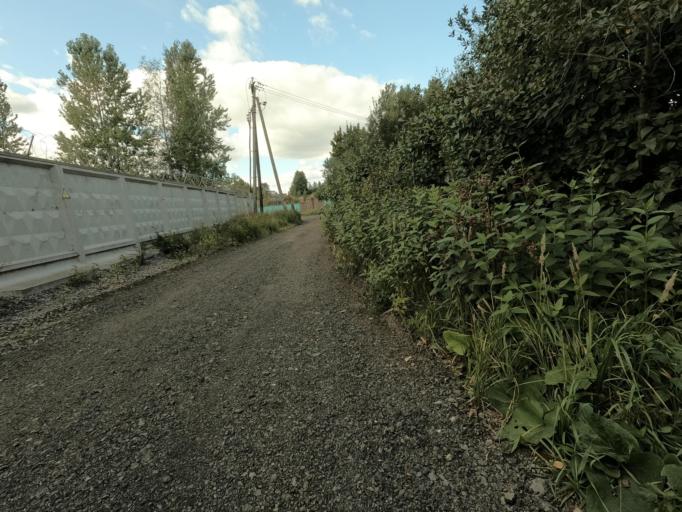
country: RU
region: St.-Petersburg
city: Krasnogvargeisky
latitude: 59.9688
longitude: 30.4959
